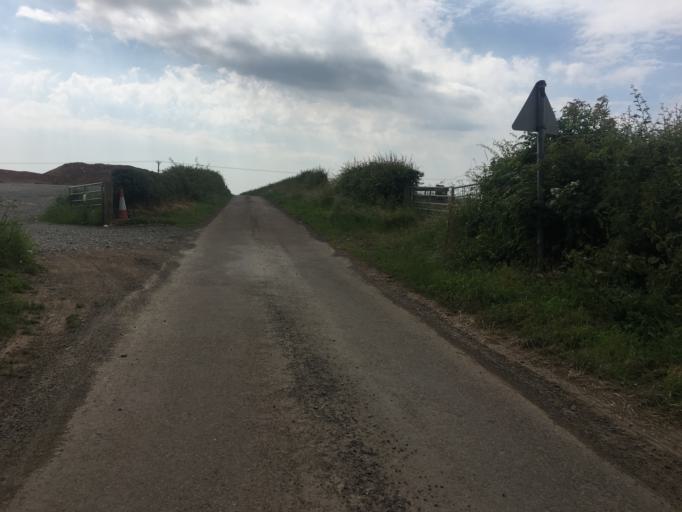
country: GB
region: England
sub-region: Northumberland
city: Belford
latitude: 55.6010
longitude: -1.7774
